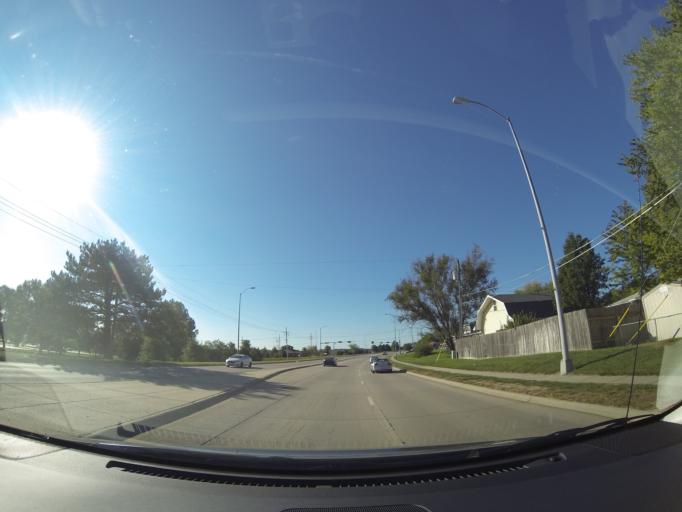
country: US
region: Nebraska
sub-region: Sarpy County
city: Gretna
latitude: 41.1409
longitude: -96.2391
